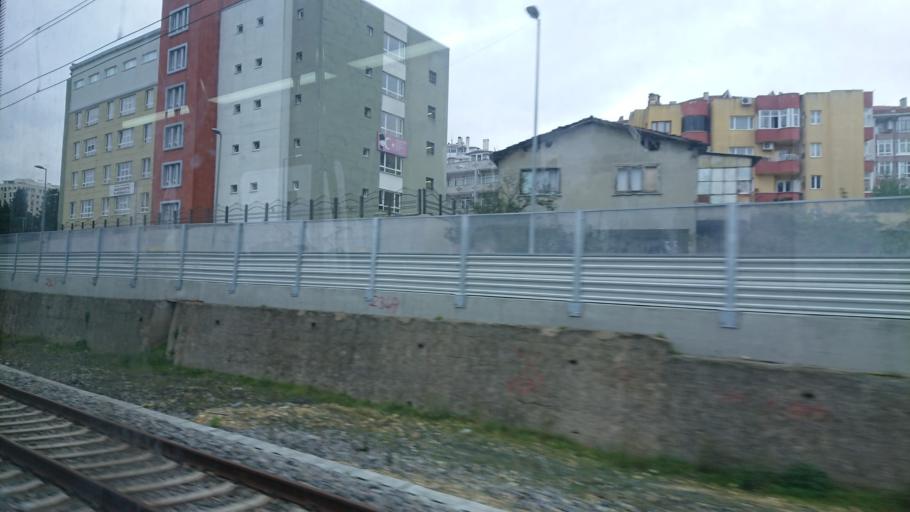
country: TR
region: Istanbul
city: Mahmutbey
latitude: 41.0021
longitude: 28.7695
